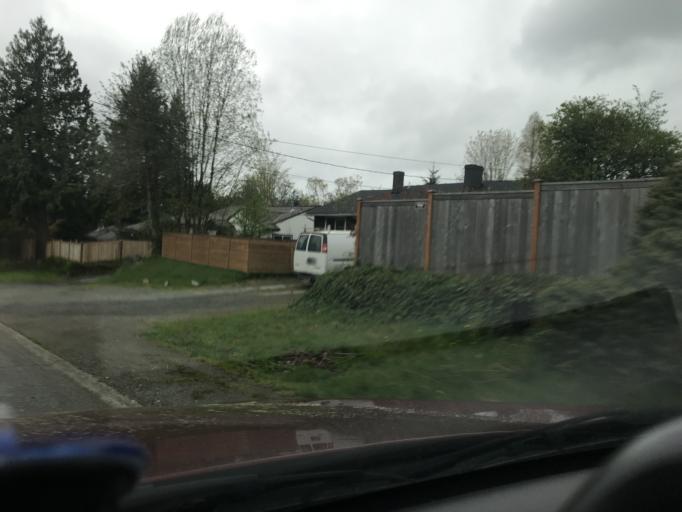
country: US
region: Washington
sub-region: King County
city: Lake Forest Park
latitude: 47.6975
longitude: -122.2961
